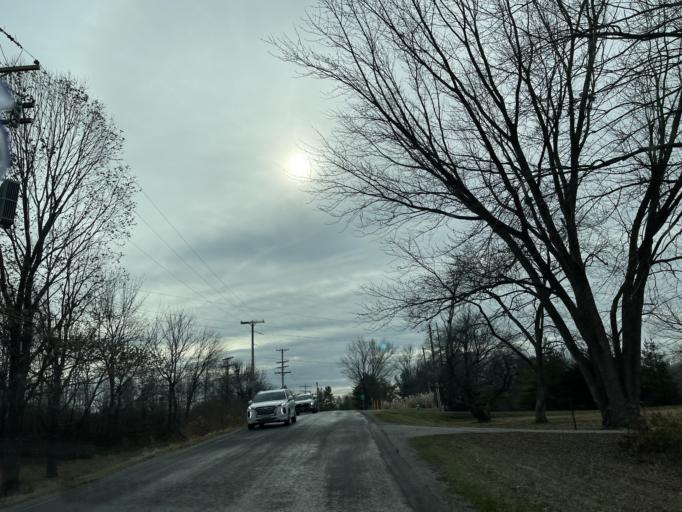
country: US
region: Illinois
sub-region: Sangamon County
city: Leland Grove
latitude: 39.7887
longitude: -89.7296
